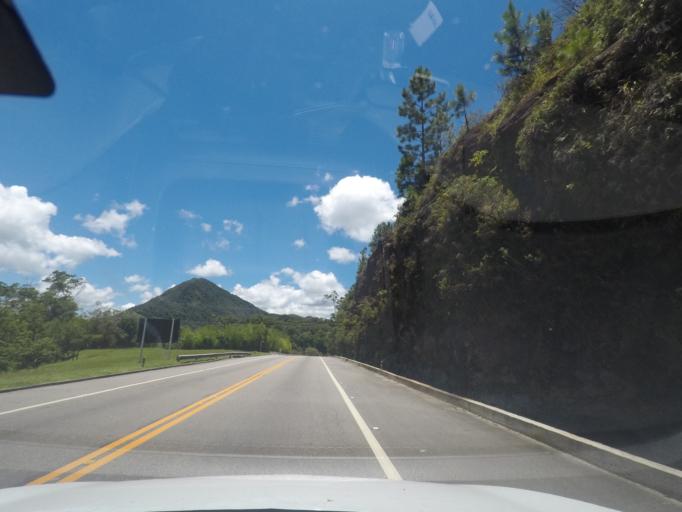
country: BR
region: Rio de Janeiro
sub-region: Teresopolis
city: Teresopolis
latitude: -22.4590
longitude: -42.9776
